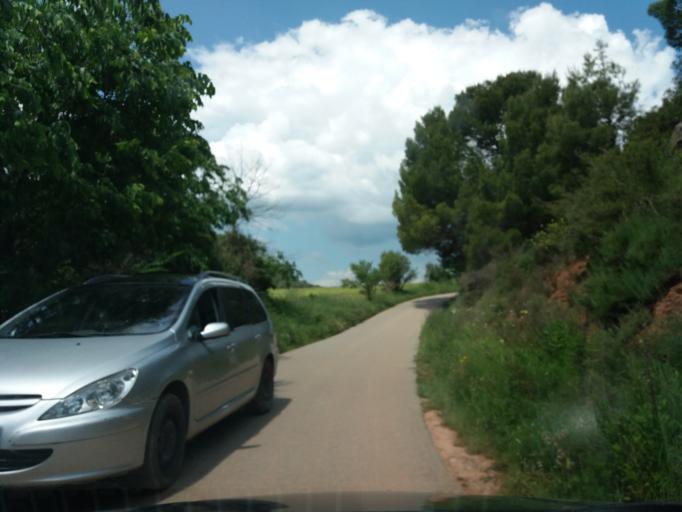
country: ES
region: Catalonia
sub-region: Provincia de Barcelona
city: Sant Joan de Vilatorrada
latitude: 41.7437
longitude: 1.7944
